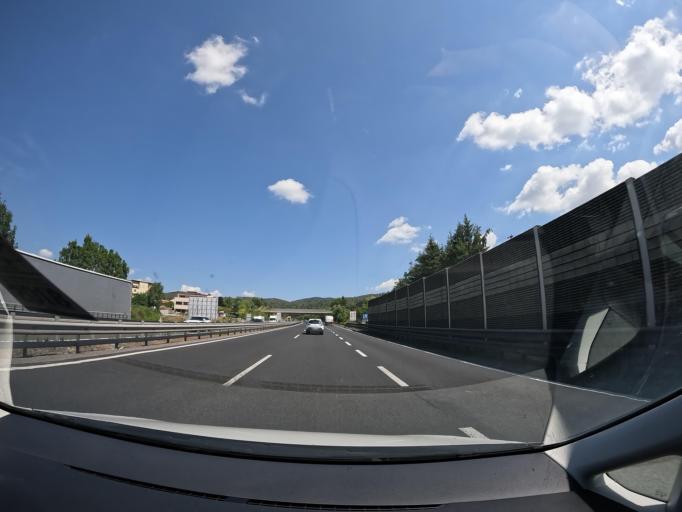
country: SI
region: Postojna
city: Postojna
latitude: 45.7638
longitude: 14.2106
